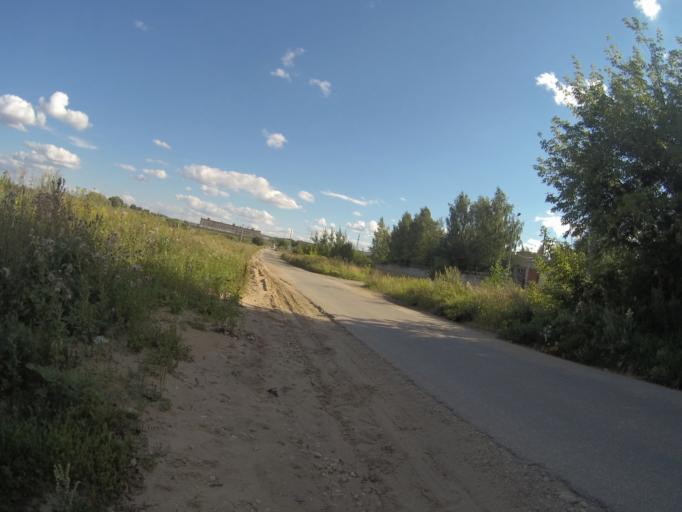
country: RU
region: Vladimir
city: Vladimir
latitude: 56.1693
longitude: 40.4156
